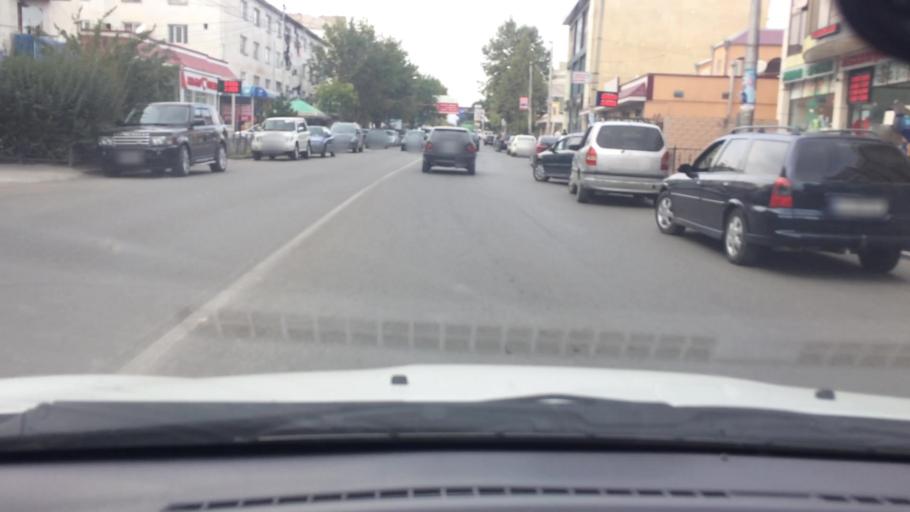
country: GE
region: Kvemo Kartli
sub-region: Marneuli
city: Marneuli
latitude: 41.4856
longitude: 44.8008
